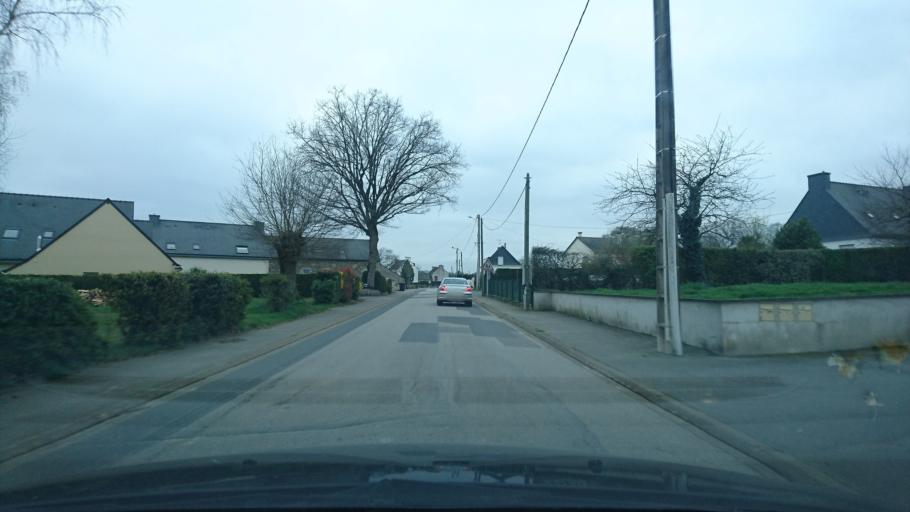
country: FR
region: Brittany
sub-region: Departement du Morbihan
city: Taupont
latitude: 47.9570
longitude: -2.4374
